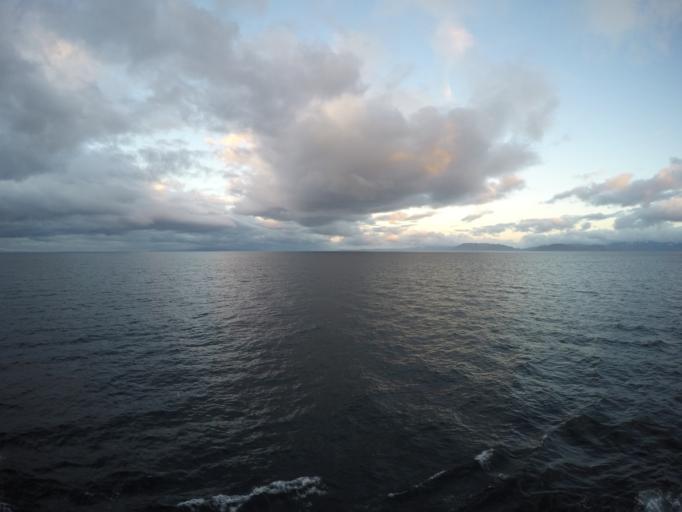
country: IS
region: West
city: Olafsvik
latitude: 65.1090
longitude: -23.3793
